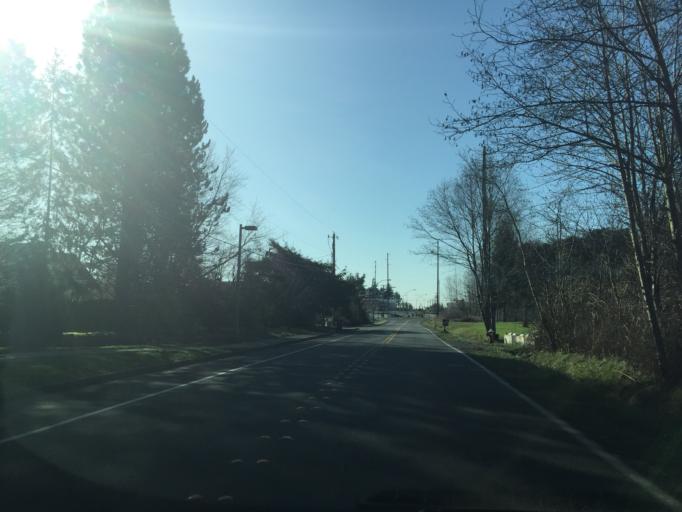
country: US
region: Washington
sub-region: Whatcom County
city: Bellingham
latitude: 48.7928
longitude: -122.5080
